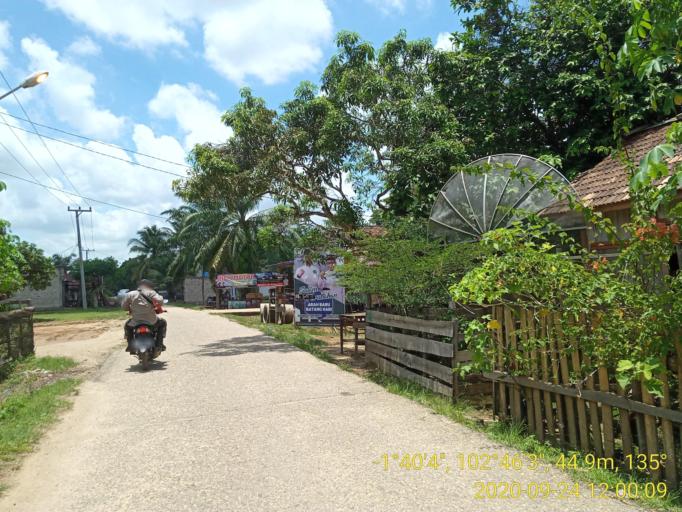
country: ID
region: Jambi
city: Sungaibengkal
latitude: -1.6678
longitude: 102.7677
